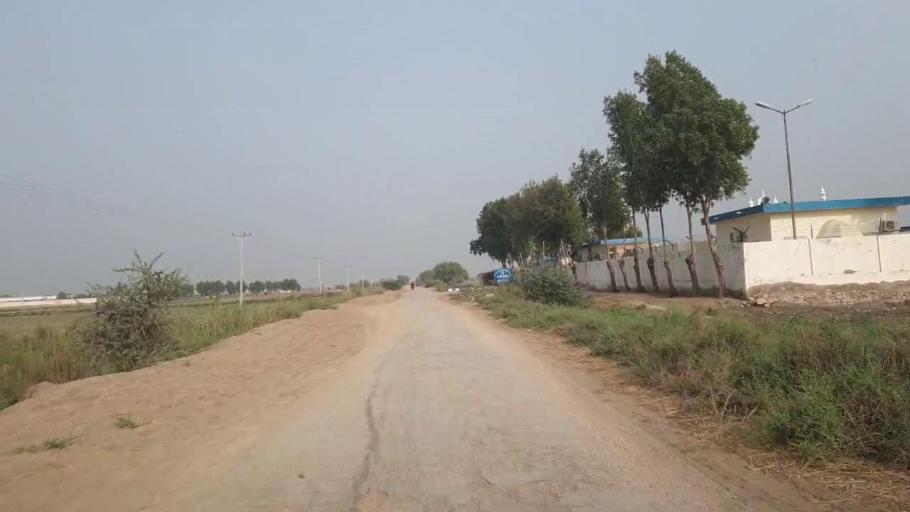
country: PK
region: Sindh
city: Mirpur Batoro
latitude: 24.5673
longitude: 68.4112
